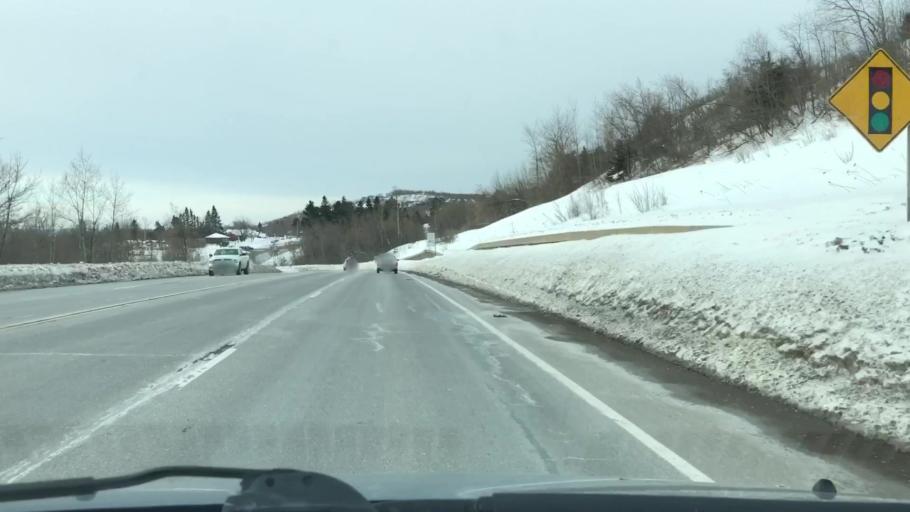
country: US
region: Minnesota
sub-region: Saint Louis County
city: Duluth
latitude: 46.7774
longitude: -92.1418
